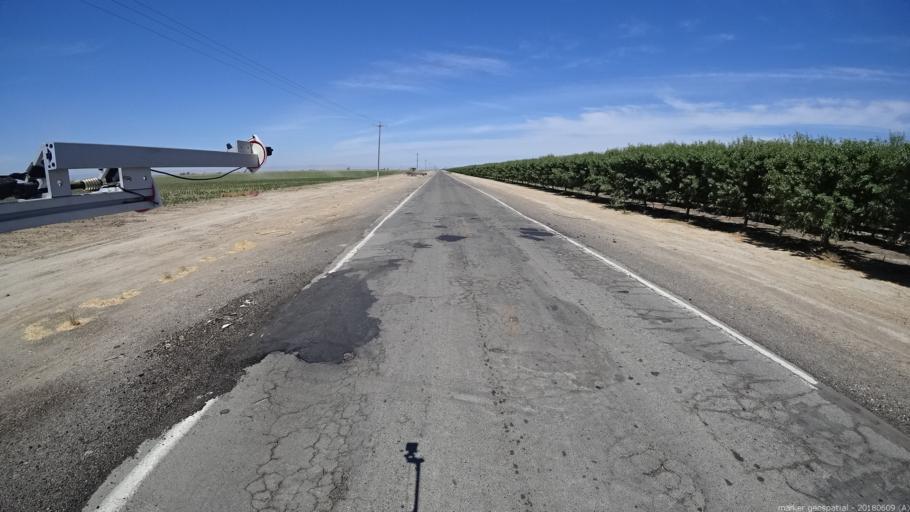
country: US
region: California
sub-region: Fresno County
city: Firebaugh
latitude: 36.9526
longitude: -120.3284
